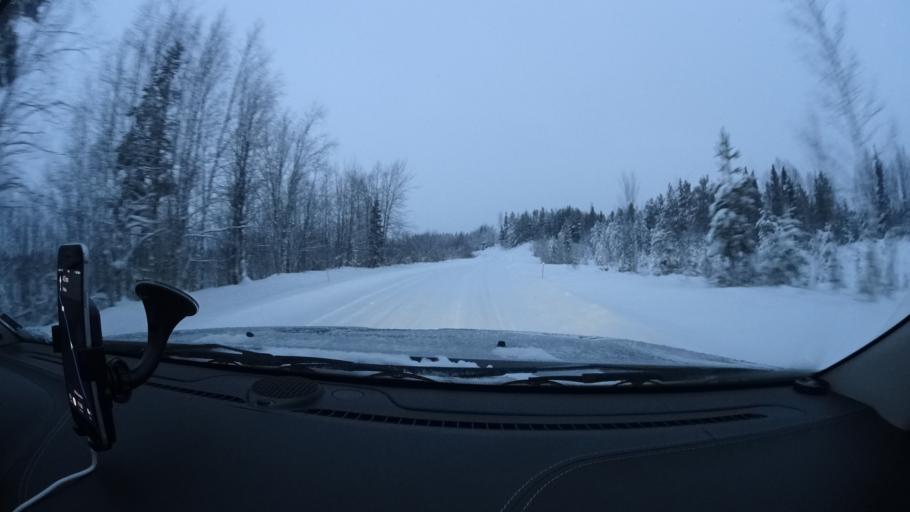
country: FI
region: Lapland
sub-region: Tunturi-Lappi
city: Kittilae
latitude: 67.9217
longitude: 25.0578
